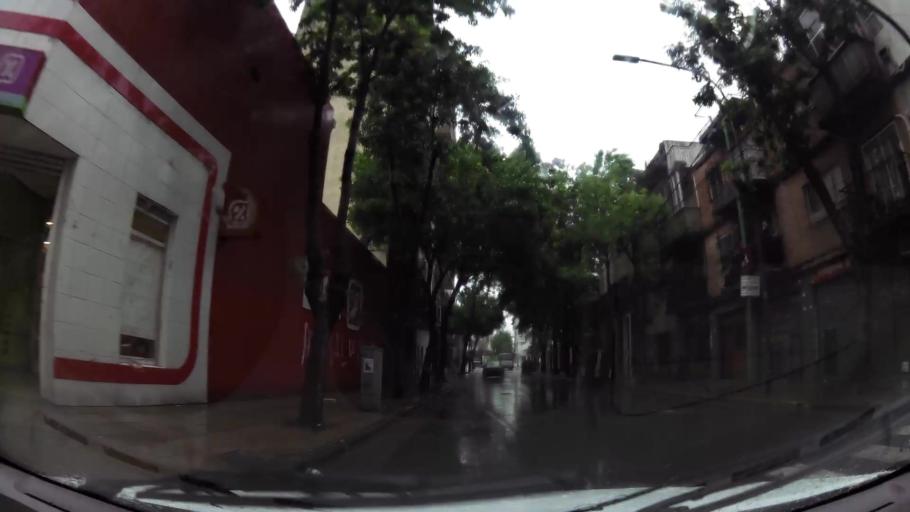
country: AR
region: Buenos Aires F.D.
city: Buenos Aires
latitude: -34.6216
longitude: -58.3901
